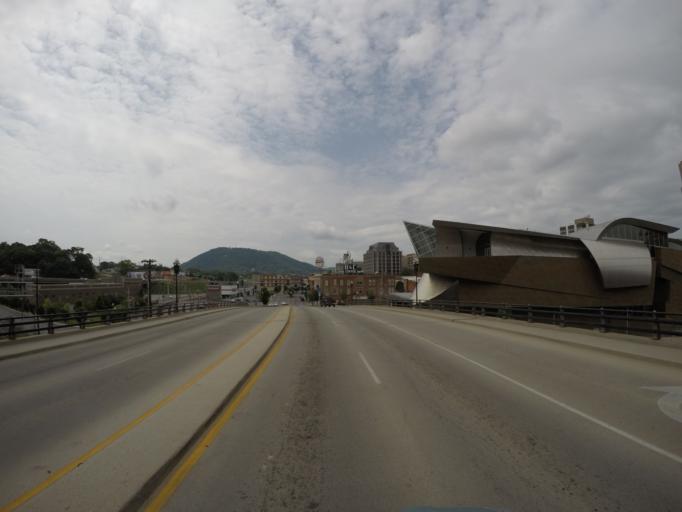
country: US
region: Virginia
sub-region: City of Roanoke
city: Roanoke
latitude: 37.2732
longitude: -79.9375
